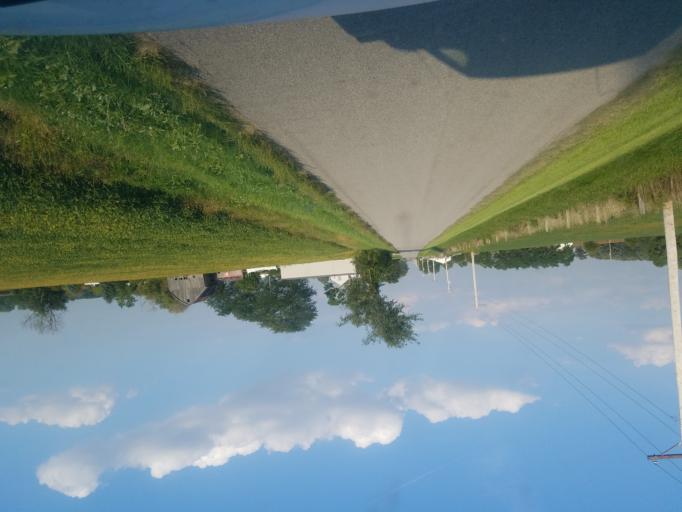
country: US
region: Ohio
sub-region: Seneca County
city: Tiffin
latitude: 40.9645
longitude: -83.0968
